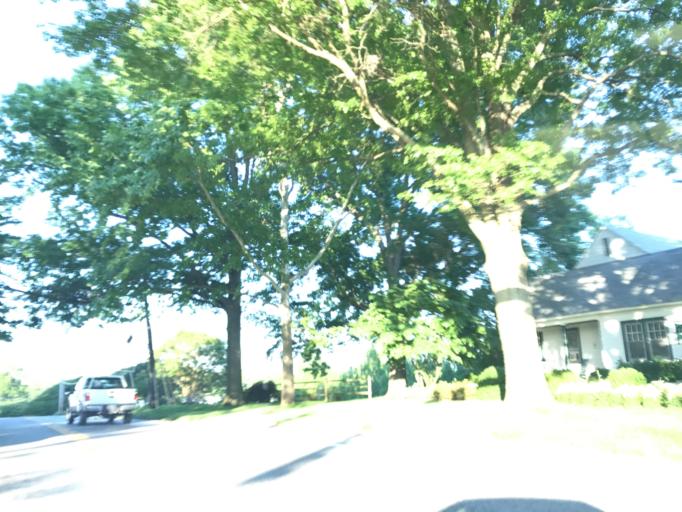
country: US
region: Maryland
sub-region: Anne Arundel County
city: Davidsonville
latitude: 38.9230
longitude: -76.6283
